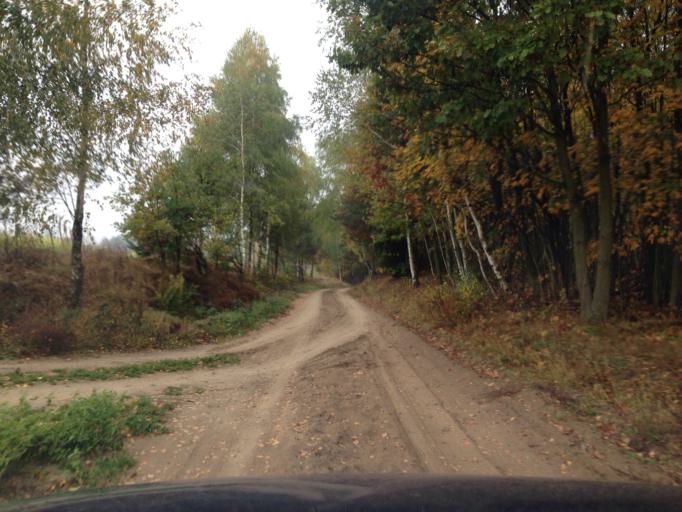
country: PL
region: Kujawsko-Pomorskie
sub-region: Powiat brodnicki
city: Gorzno
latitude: 53.2722
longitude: 19.7073
